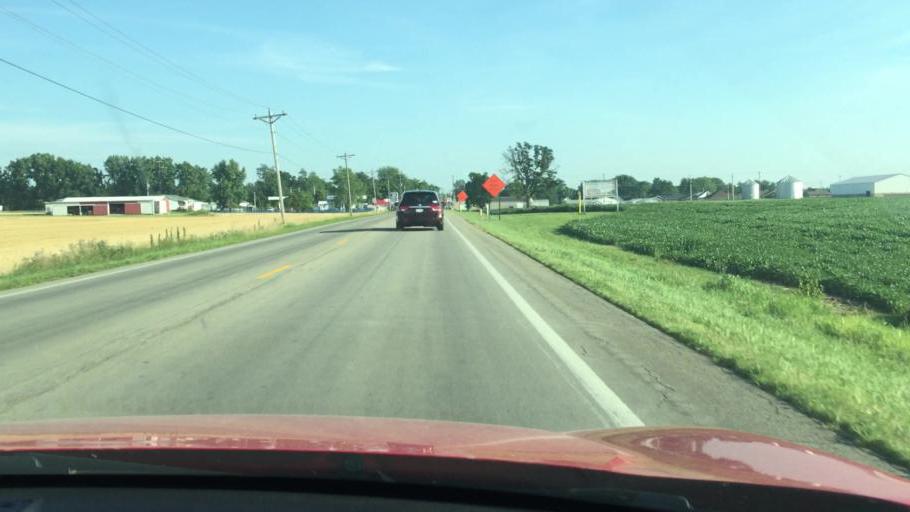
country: US
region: Ohio
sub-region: Logan County
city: Northwood
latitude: 40.4508
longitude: -83.8073
